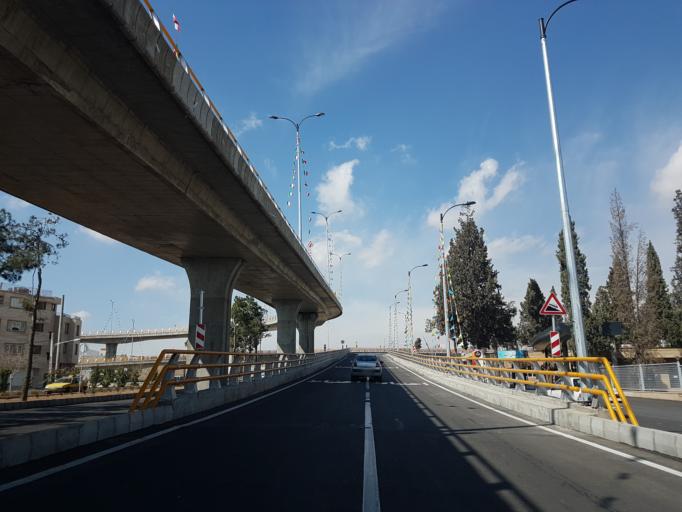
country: IR
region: Fars
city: Shiraz
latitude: 29.6112
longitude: 52.4698
